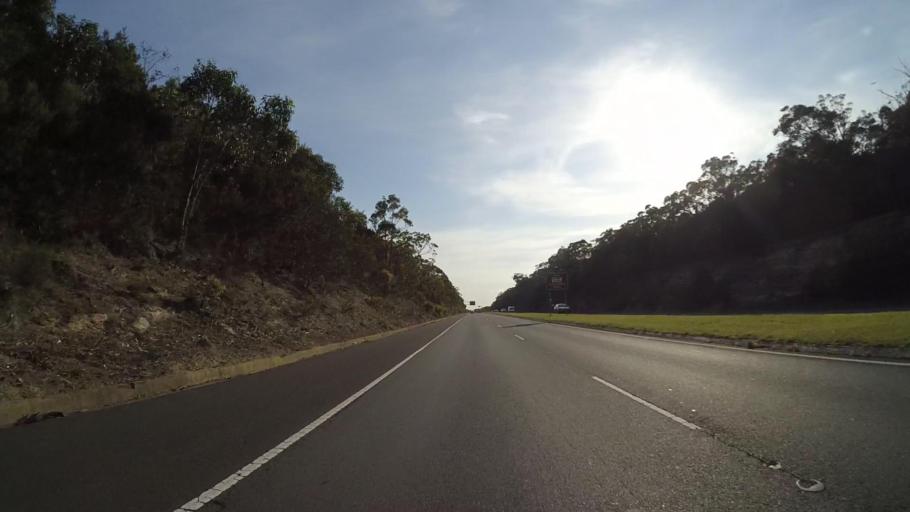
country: AU
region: New South Wales
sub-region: Sutherland Shire
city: Loftus
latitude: -34.0555
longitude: 151.0430
